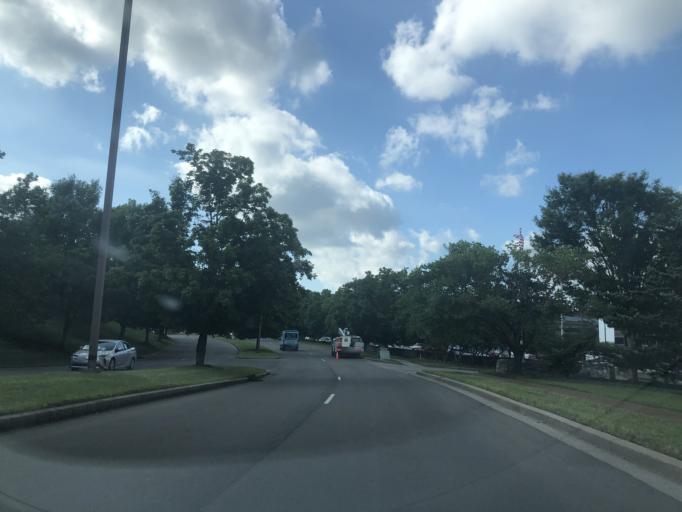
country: US
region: Tennessee
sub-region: Davidson County
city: Forest Hills
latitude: 36.0937
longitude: -86.8223
